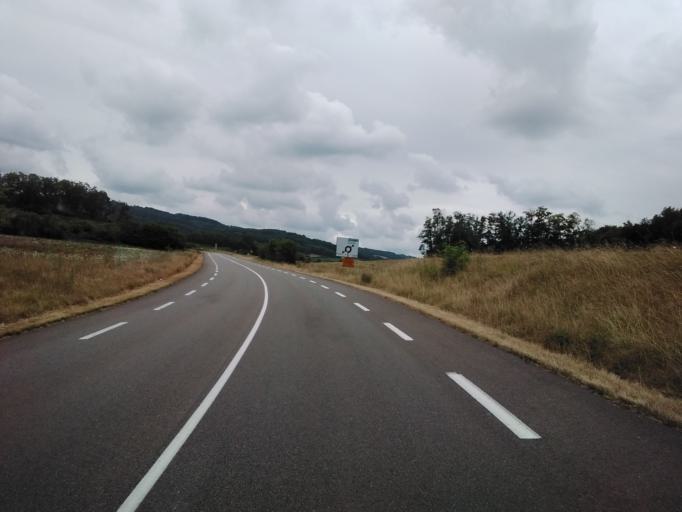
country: FR
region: Franche-Comte
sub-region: Departement du Jura
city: Montmorot
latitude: 46.6554
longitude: 5.5075
